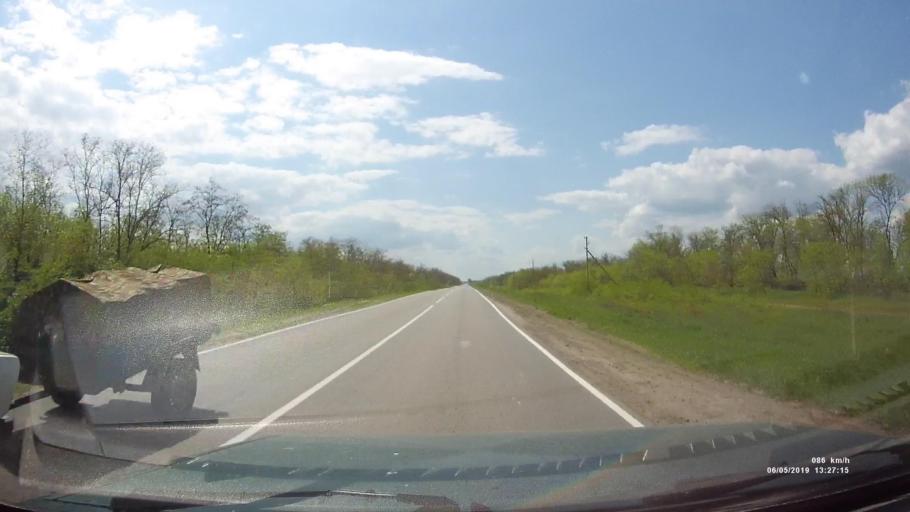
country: RU
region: Rostov
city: Ust'-Donetskiy
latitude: 47.6733
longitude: 40.8835
